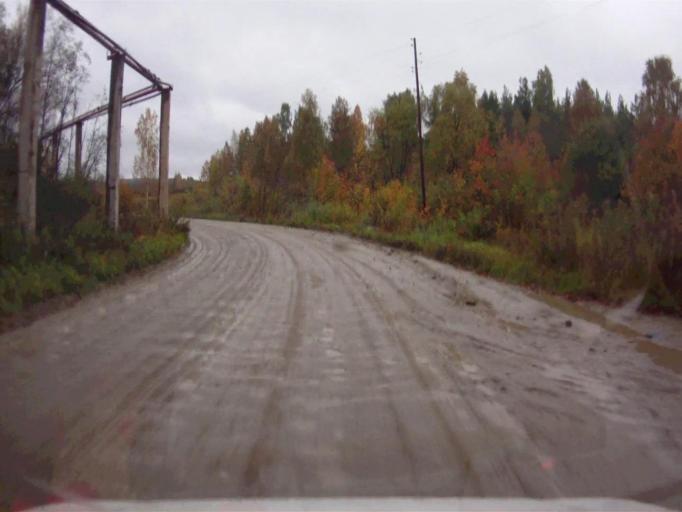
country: RU
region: Chelyabinsk
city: Kyshtym
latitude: 55.7310
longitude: 60.5197
